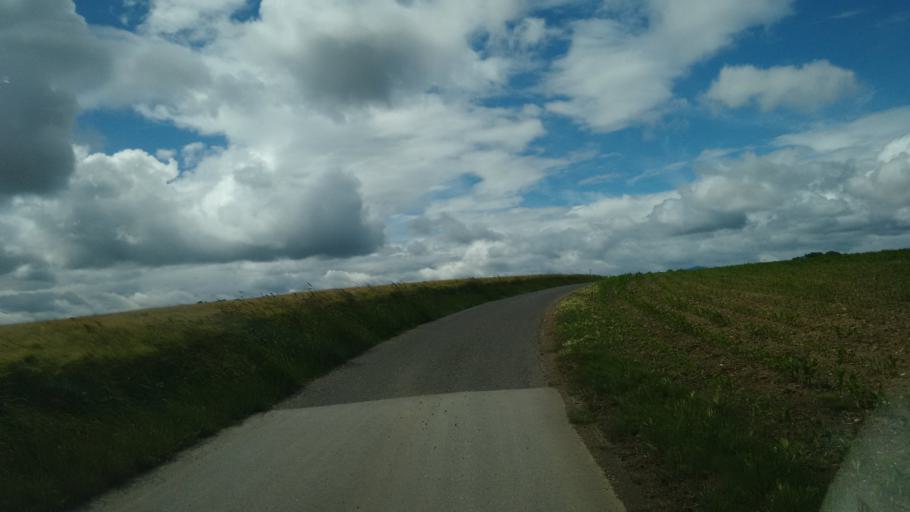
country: AT
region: Upper Austria
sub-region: Politischer Bezirk Steyr-Land
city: Pfarrkirchen bei Bad Hall
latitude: 48.0126
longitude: 14.1659
